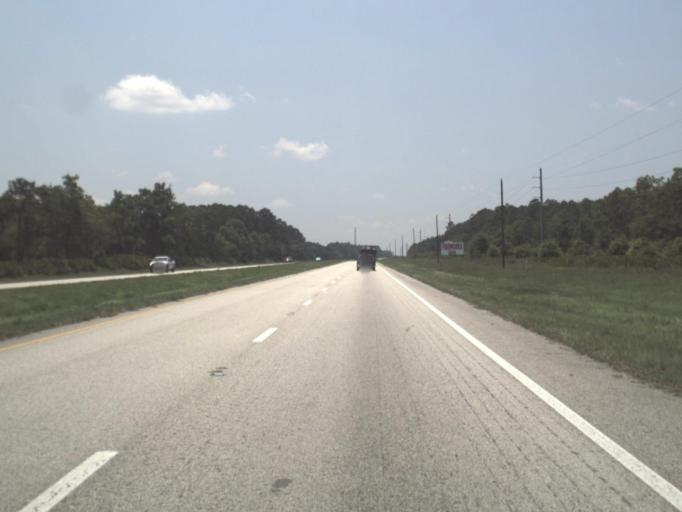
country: US
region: Florida
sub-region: Baker County
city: Macclenny
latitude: 30.1357
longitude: -82.0390
